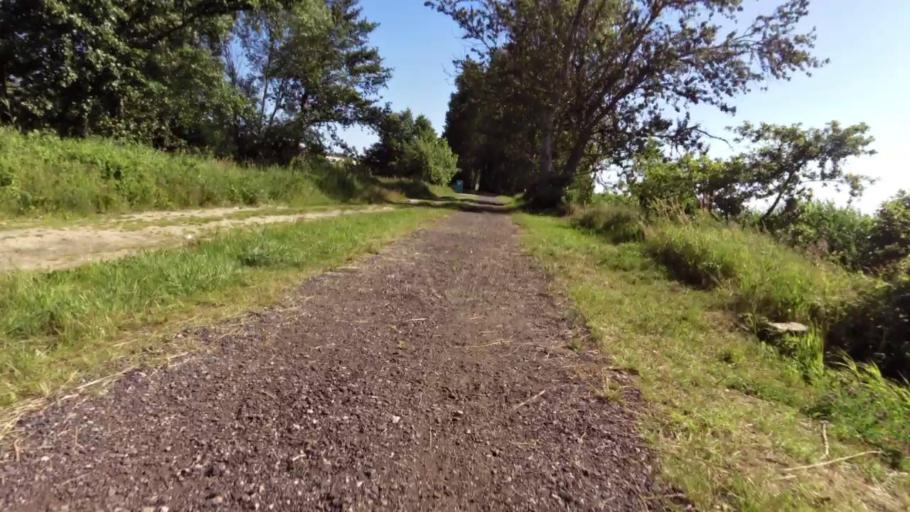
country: PL
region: West Pomeranian Voivodeship
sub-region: Powiat koszalinski
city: Mielno
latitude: 54.2748
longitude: 16.1176
